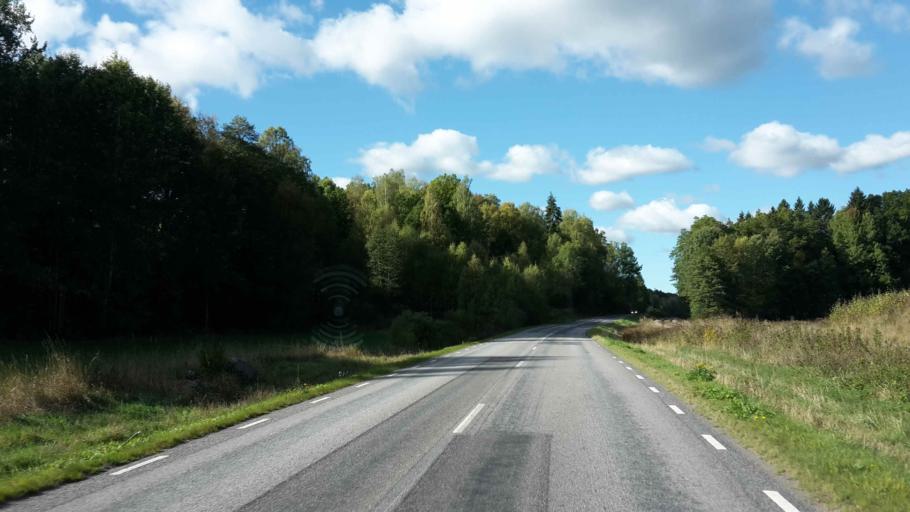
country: SE
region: OEstergoetland
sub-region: Atvidabergs Kommun
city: Atvidaberg
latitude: 58.1508
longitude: 16.1710
